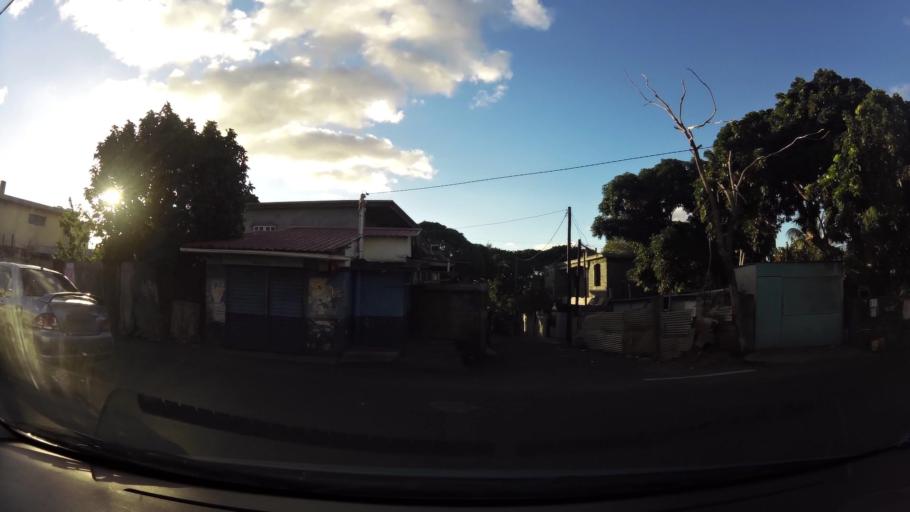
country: MU
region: Plaines Wilhems
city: Quatre Bornes
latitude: -20.2450
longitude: 57.4617
